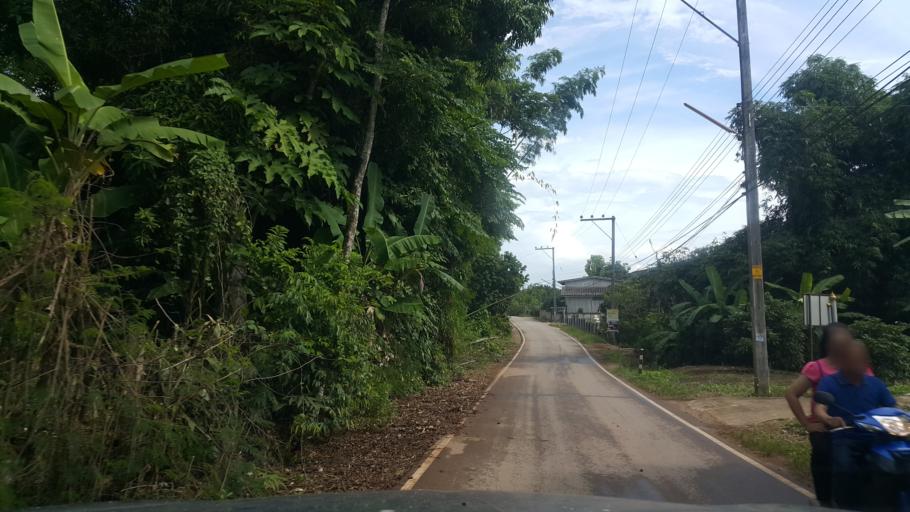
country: TH
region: Chiang Mai
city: Mae Taeng
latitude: 19.1981
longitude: 99.0014
